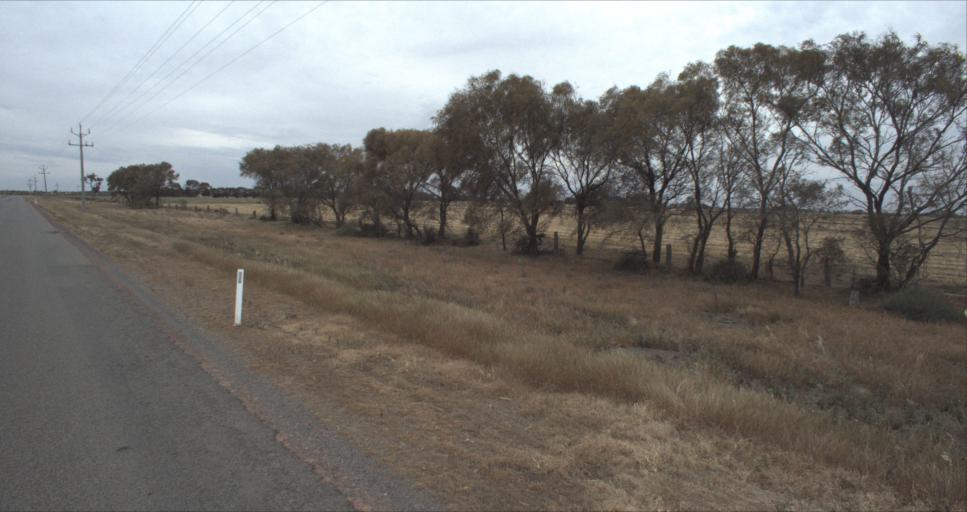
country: AU
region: New South Wales
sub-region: Leeton
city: Leeton
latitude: -34.4962
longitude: 146.4005
